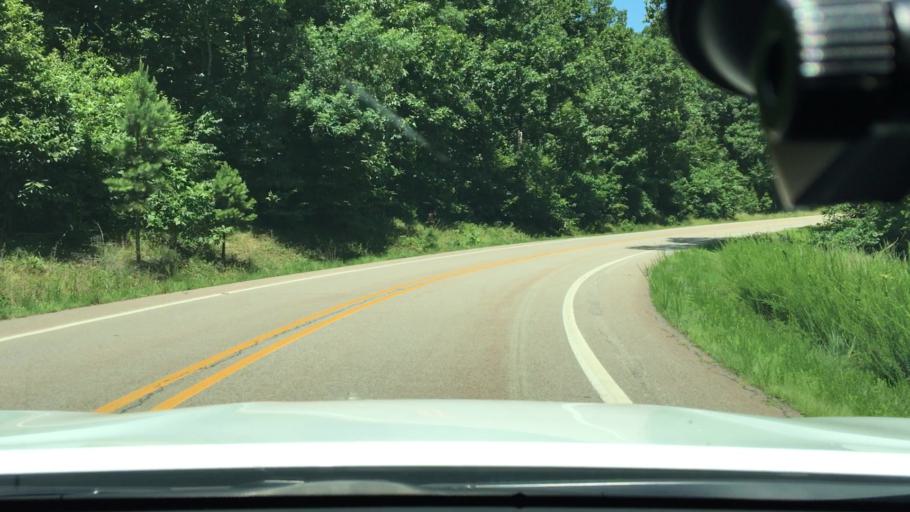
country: US
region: Arkansas
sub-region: Logan County
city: Paris
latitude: 35.1673
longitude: -93.6404
